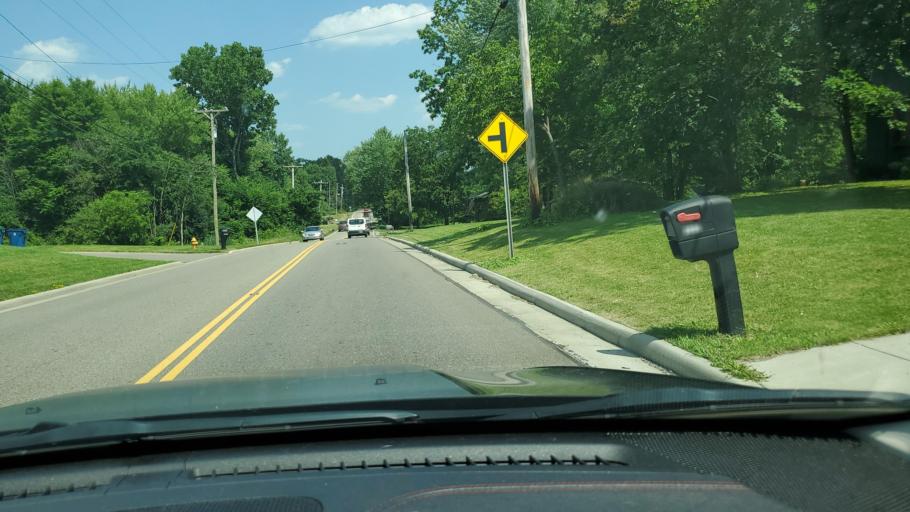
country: US
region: Ohio
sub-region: Trumbull County
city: McKinley Heights
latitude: 41.1821
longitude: -80.7154
